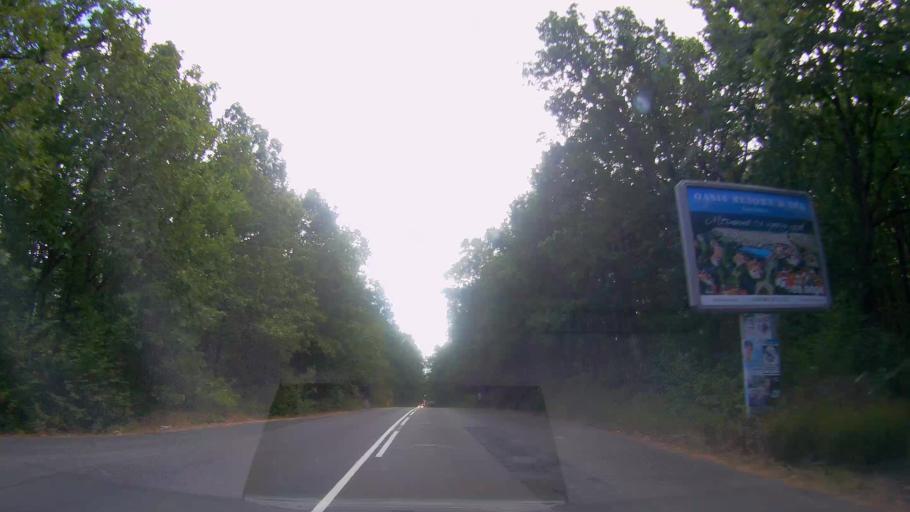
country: BG
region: Burgas
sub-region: Obshtina Primorsko
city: Primorsko
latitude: 42.2835
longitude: 27.7373
